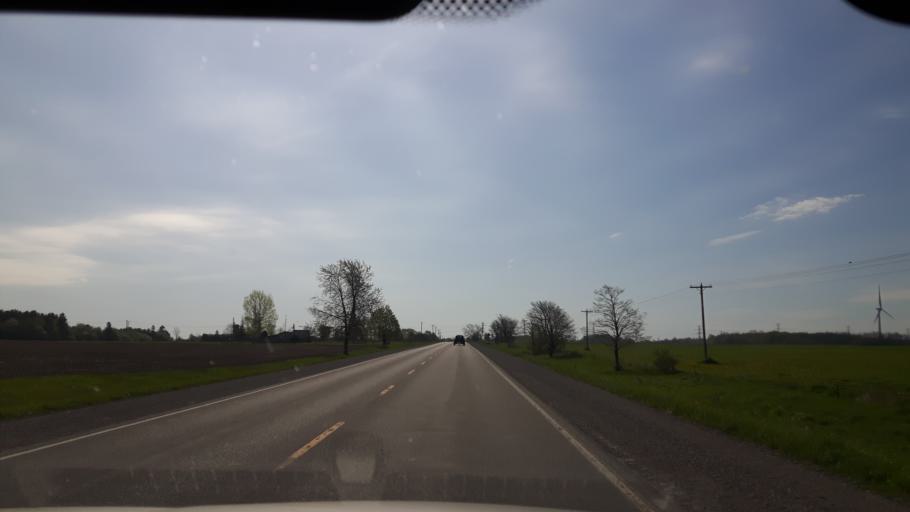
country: CA
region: Ontario
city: Bluewater
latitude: 43.5479
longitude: -81.6548
